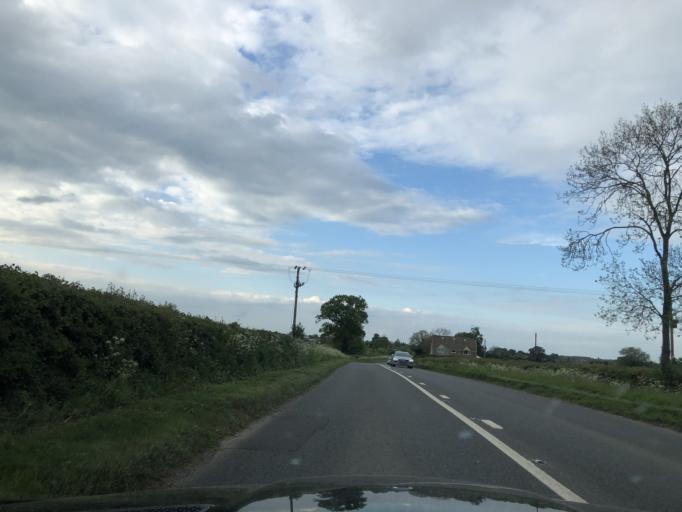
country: GB
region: England
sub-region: Gloucestershire
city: Moreton in Marsh
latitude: 51.9764
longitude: -1.7073
